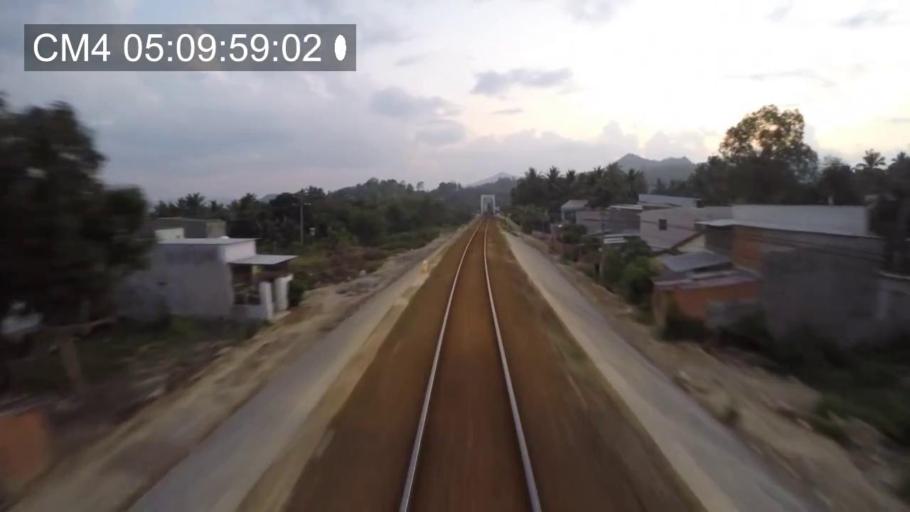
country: VN
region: Khanh Hoa
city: Nha Trang
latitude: 12.3053
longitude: 109.1860
